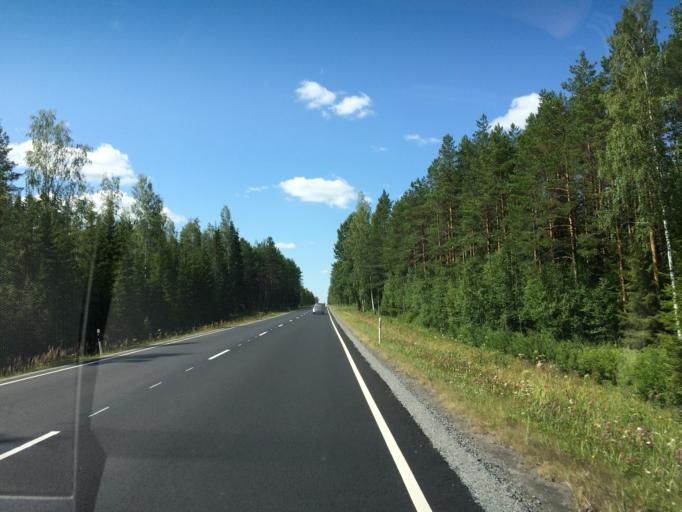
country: FI
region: Pirkanmaa
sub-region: Lounais-Pirkanmaa
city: Kiikoinen
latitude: 61.4741
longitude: 22.4919
